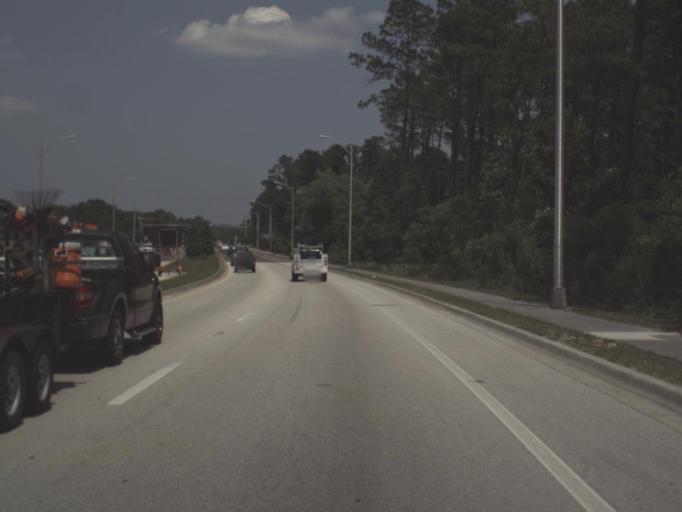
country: US
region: Florida
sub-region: Duval County
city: Jacksonville
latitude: 30.3524
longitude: -81.5462
